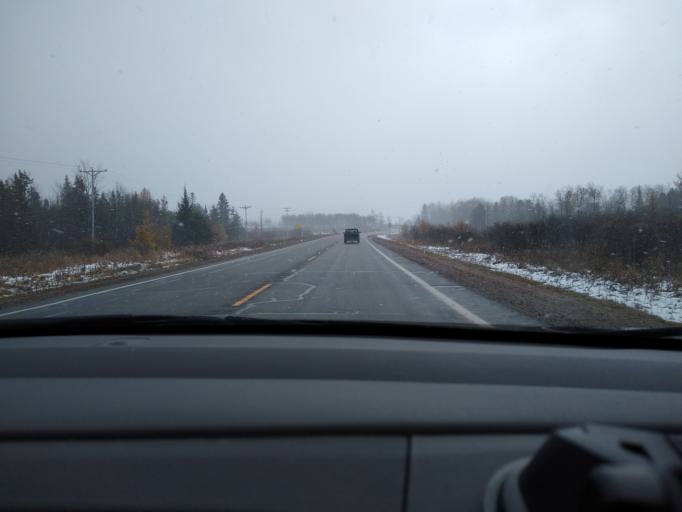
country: US
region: Wisconsin
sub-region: Florence County
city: Florence
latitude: 46.0821
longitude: -88.0750
